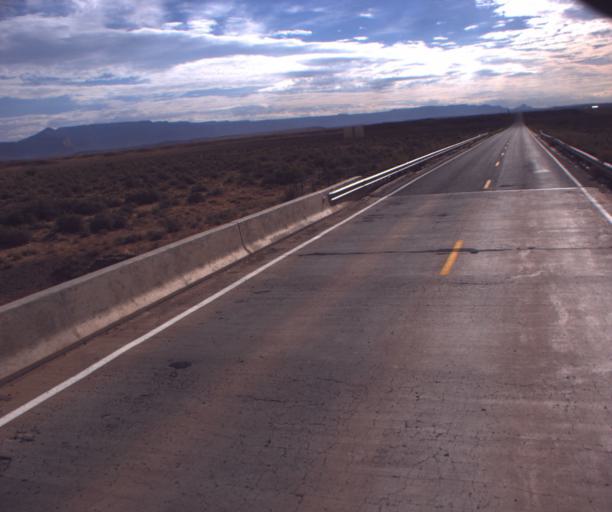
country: US
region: Arizona
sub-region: Apache County
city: Many Farms
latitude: 36.5306
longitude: -109.5069
